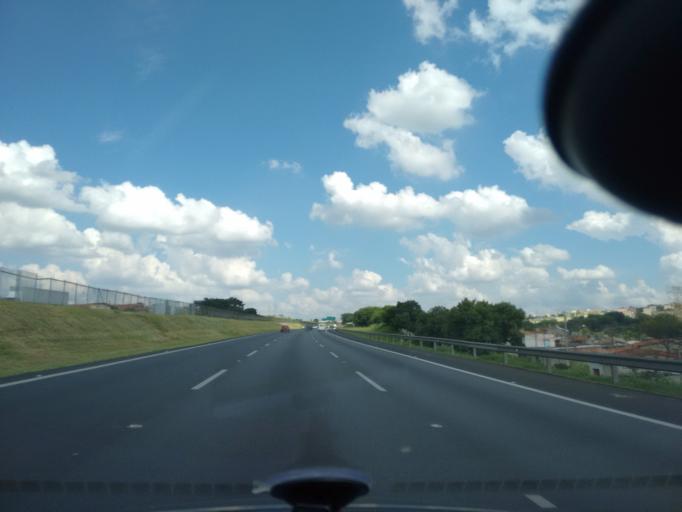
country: BR
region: Sao Paulo
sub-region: Campinas
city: Campinas
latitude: -22.9688
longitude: -47.1180
